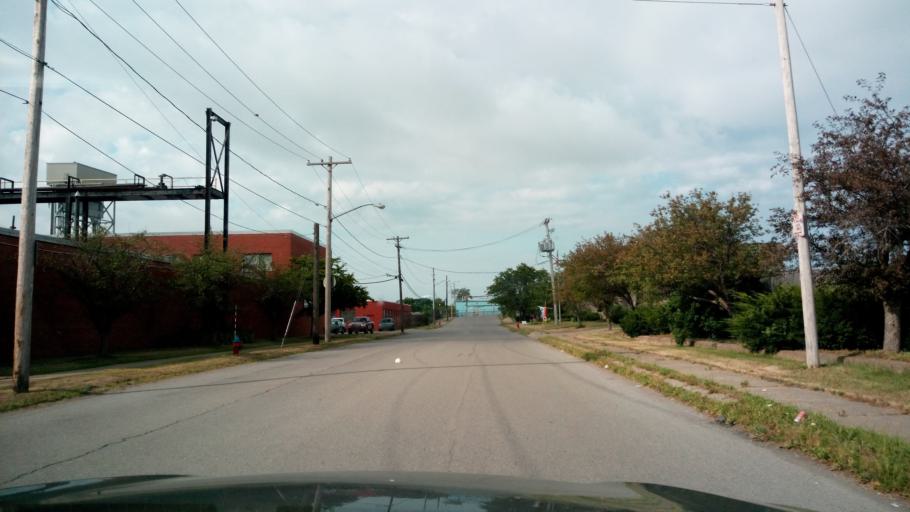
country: US
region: New York
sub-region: Erie County
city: Buffalo
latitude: 42.8653
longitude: -78.8427
